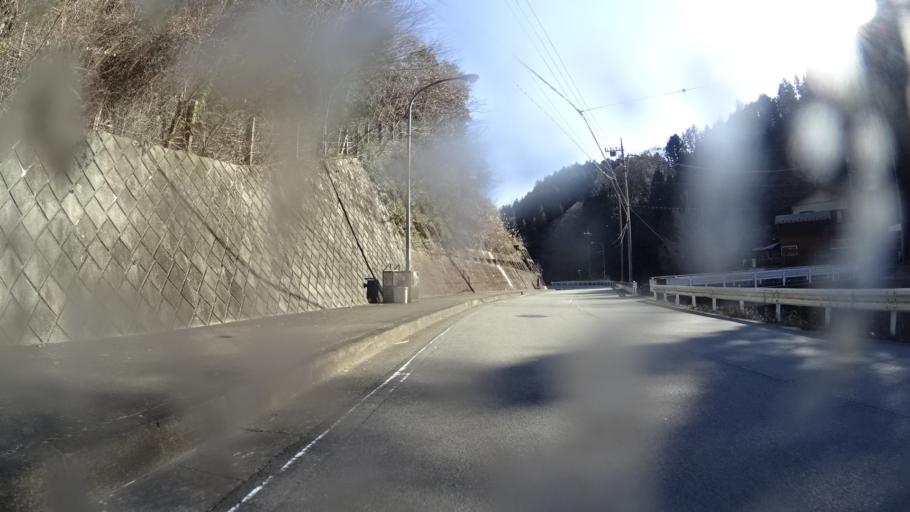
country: JP
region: Yamanashi
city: Uenohara
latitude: 35.6322
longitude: 139.1427
